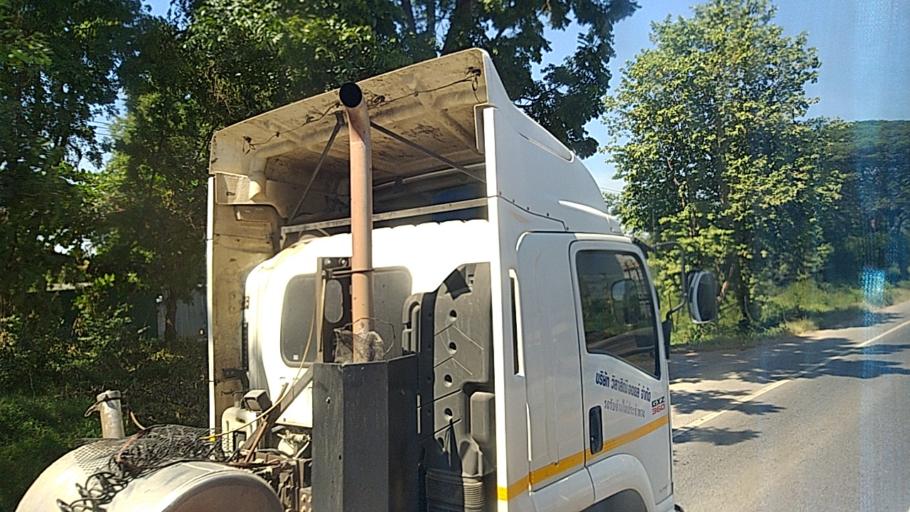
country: TH
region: Khon Kaen
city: Ban Haet
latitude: 16.3133
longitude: 102.7923
